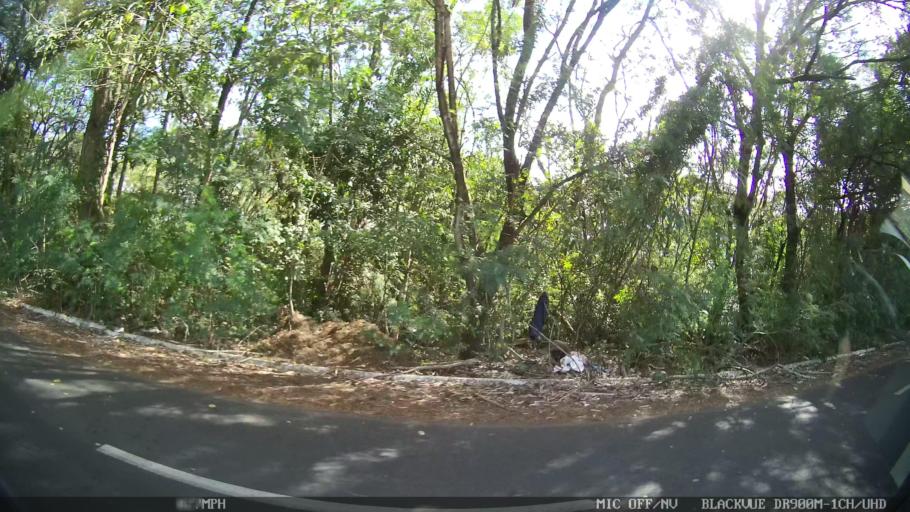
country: BR
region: Sao Paulo
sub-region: Americana
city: Americana
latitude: -22.7314
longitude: -47.3291
